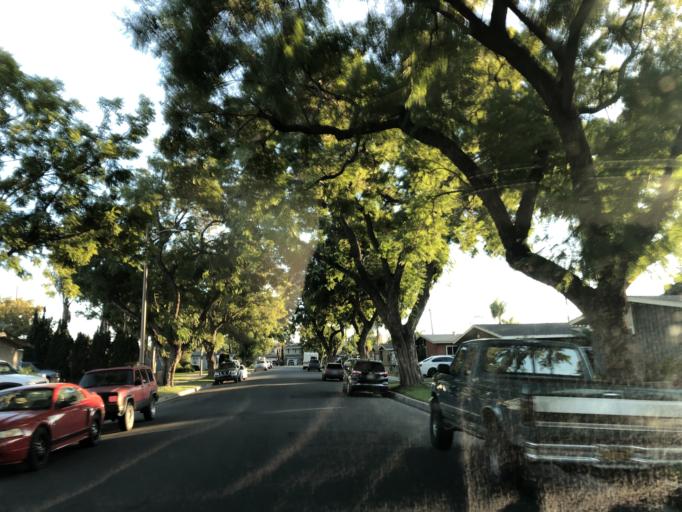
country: US
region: California
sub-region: Orange County
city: Tustin
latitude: 33.7543
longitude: -117.8457
